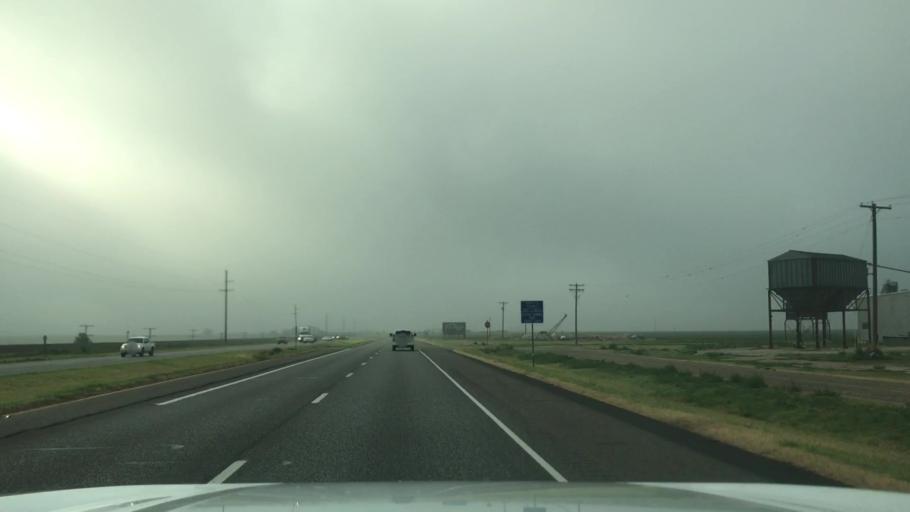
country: US
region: Texas
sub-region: Lubbock County
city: Ransom Canyon
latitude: 33.4817
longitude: -101.7092
